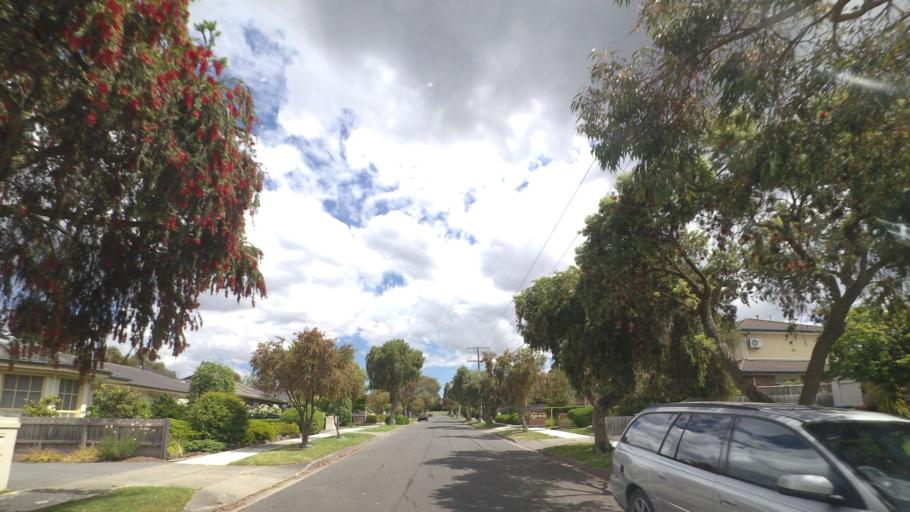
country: AU
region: Victoria
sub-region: Knox
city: Wantirna
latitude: -37.8482
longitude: 145.2363
